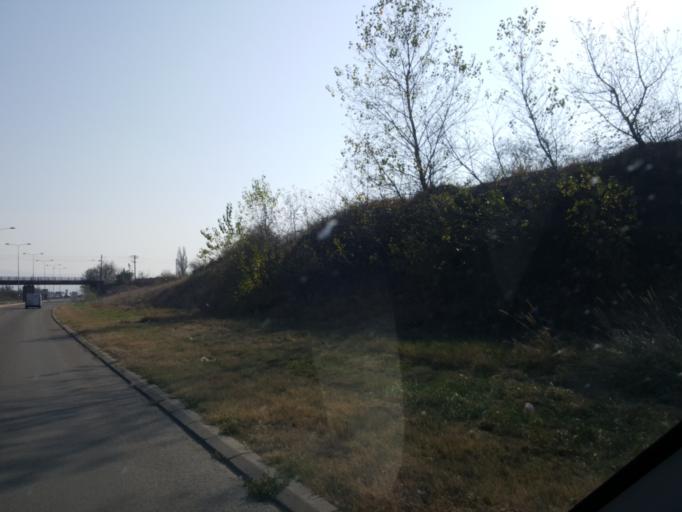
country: RS
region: Central Serbia
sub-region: Nisavski Okrug
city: Nis
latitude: 43.3212
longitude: 21.8273
